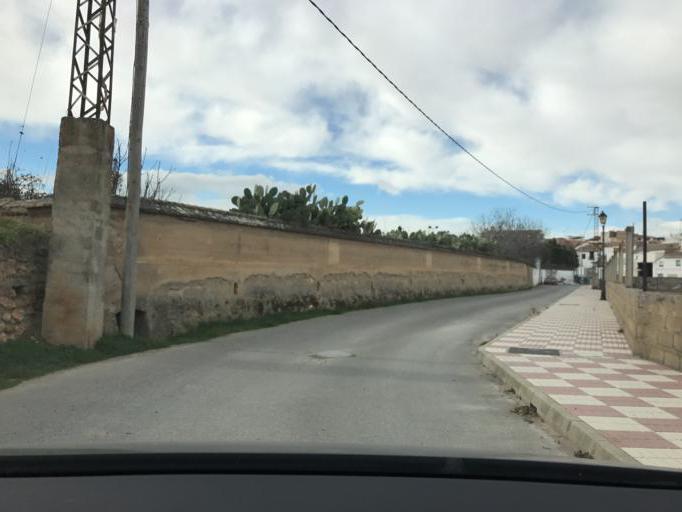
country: ES
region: Andalusia
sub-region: Provincia de Granada
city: Otura
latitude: 37.0930
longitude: -3.6315
